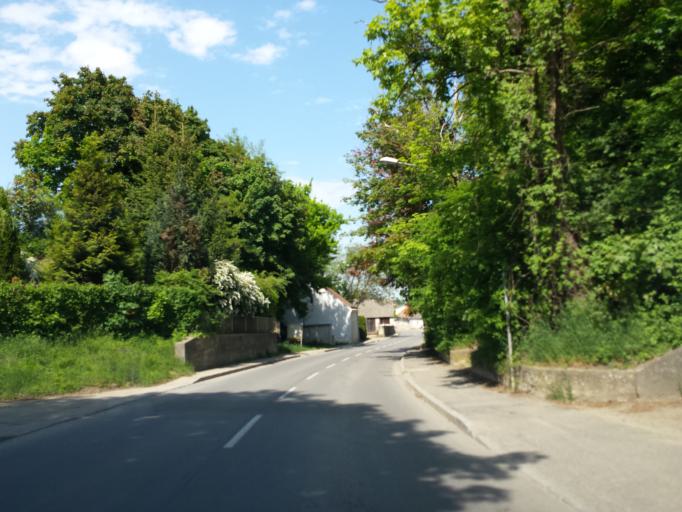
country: AT
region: Lower Austria
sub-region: Politischer Bezirk Tulln
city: Atzenbrugg
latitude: 48.3028
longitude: 15.8966
